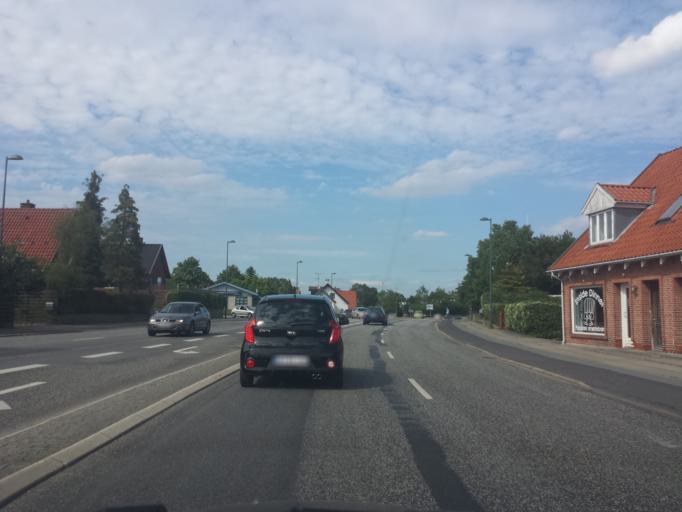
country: DK
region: Capital Region
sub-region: Ballerup Kommune
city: Ballerup
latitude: 55.7251
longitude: 12.3561
